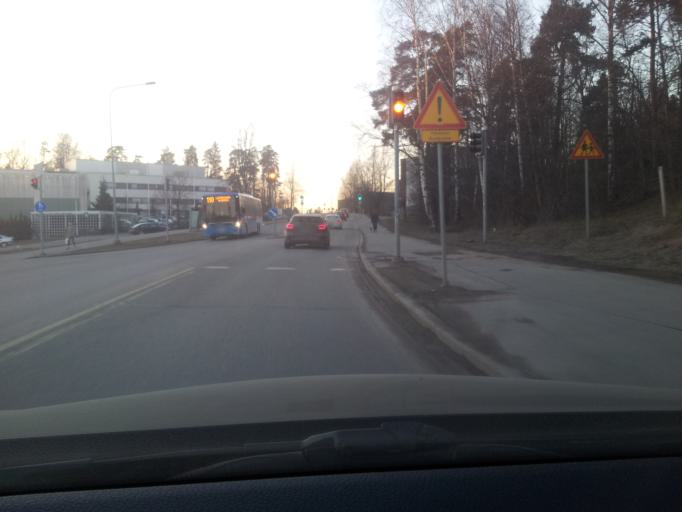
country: FI
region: Uusimaa
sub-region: Helsinki
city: Kilo
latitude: 60.2213
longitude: 24.8074
